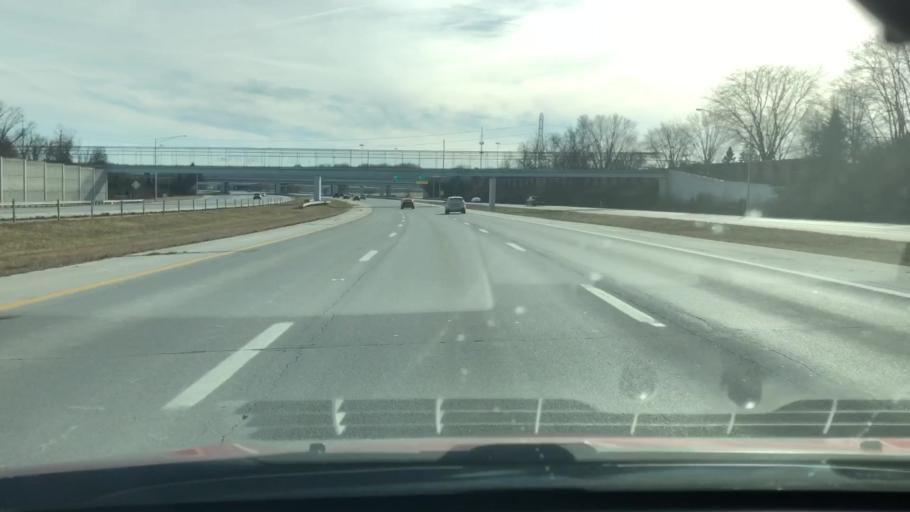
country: US
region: Ohio
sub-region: Greene County
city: Beavercreek
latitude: 39.7432
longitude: -84.0945
